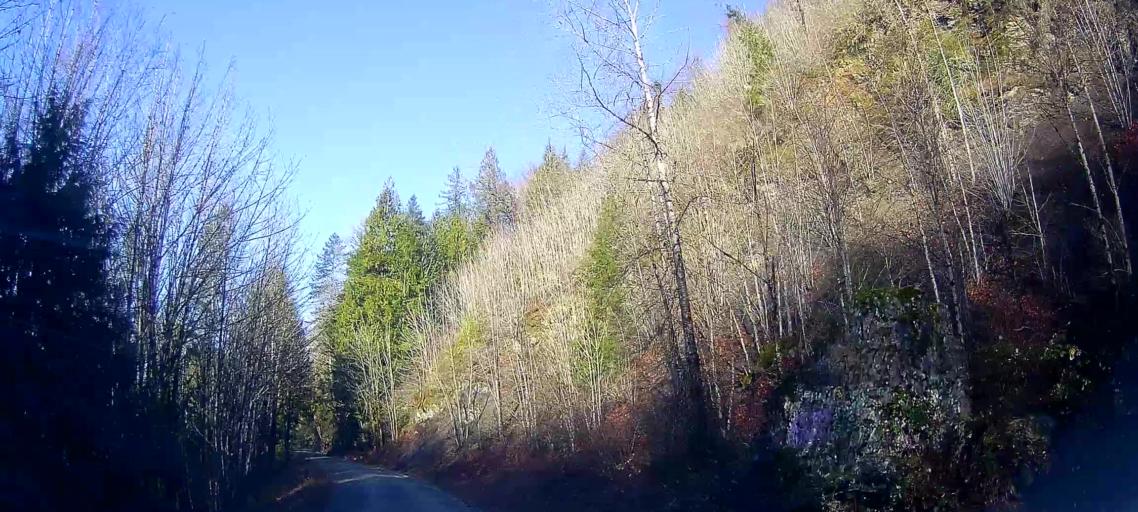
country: US
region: Washington
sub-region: Snohomish County
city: Darrington
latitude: 48.5497
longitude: -121.7263
